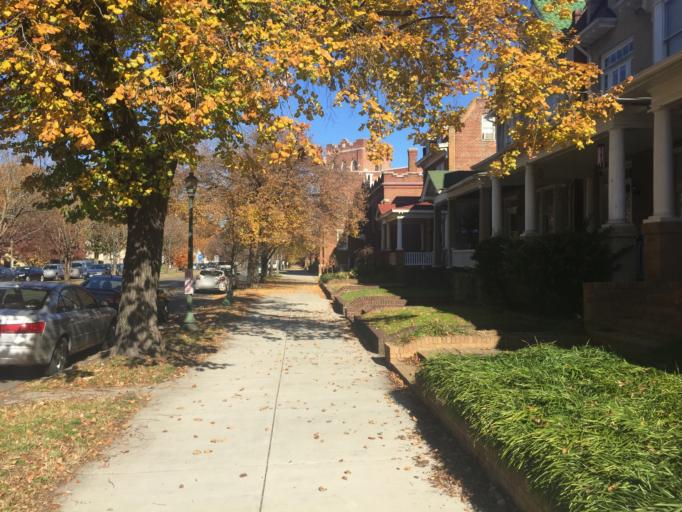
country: US
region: Virginia
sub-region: City of Richmond
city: Richmond
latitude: 37.5541
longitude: -77.4747
